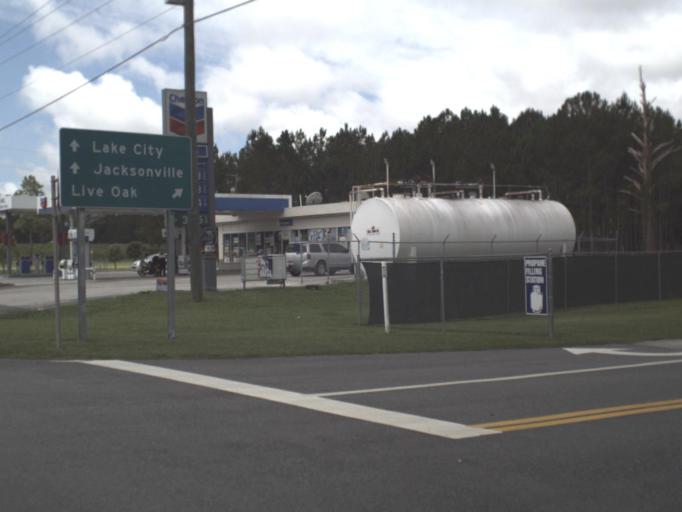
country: US
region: Florida
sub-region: Columbia County
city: Five Points
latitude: 30.2441
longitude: -82.6384
